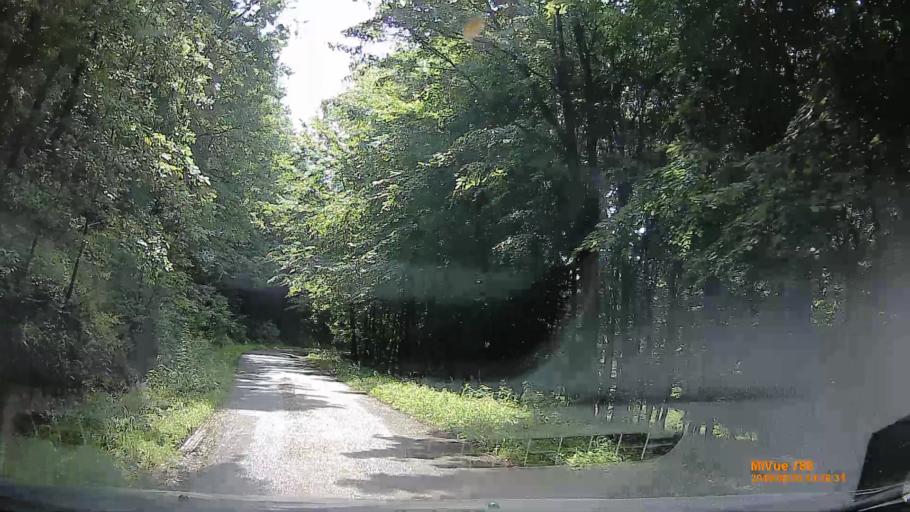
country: HU
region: Baranya
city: Hidas
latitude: 46.1999
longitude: 18.5372
